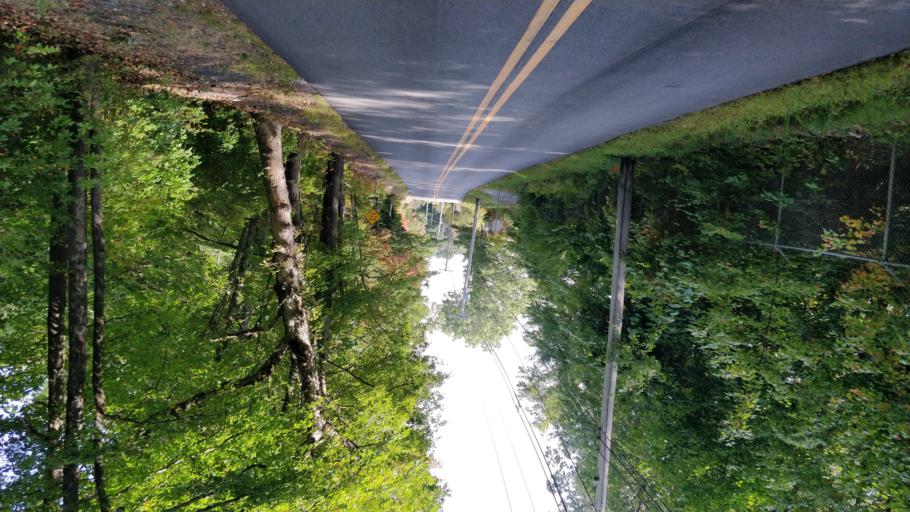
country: US
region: Massachusetts
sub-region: Bristol County
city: Norton
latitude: 41.9449
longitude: -71.2337
